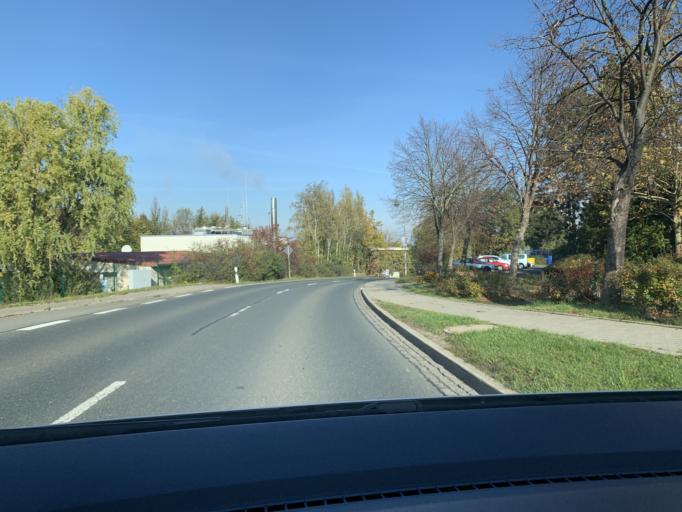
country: DE
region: Thuringia
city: Schmolln
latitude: 50.8873
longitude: 12.3496
